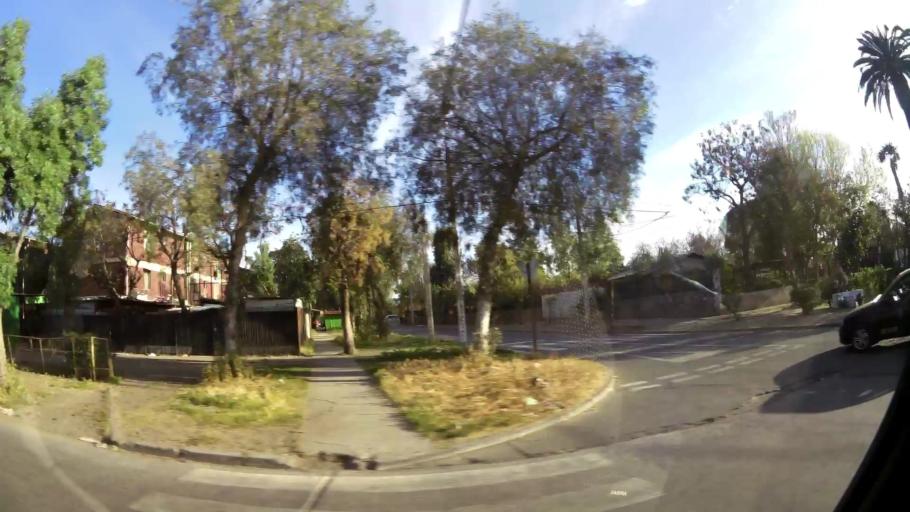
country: CL
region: Santiago Metropolitan
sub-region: Provincia de Santiago
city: Lo Prado
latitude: -33.4369
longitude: -70.7196
